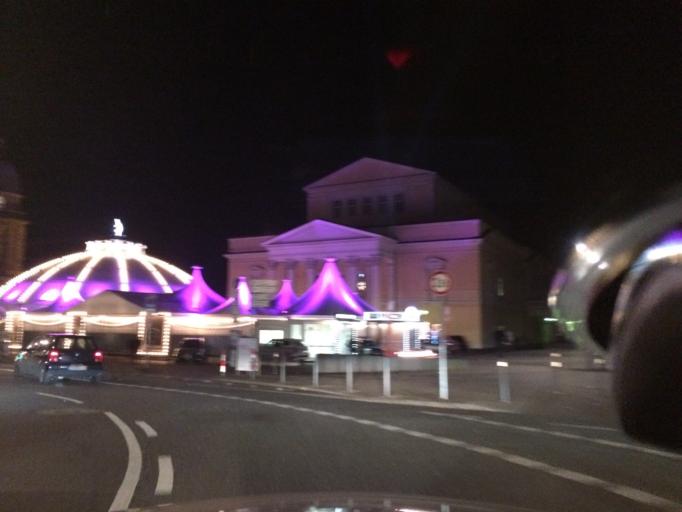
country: DE
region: Hesse
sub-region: Regierungsbezirk Darmstadt
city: Darmstadt
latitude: 49.8745
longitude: 8.6560
